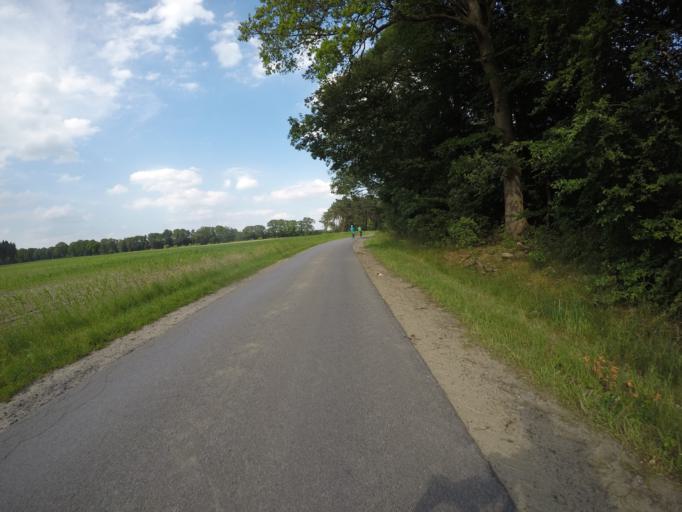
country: DE
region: North Rhine-Westphalia
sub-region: Regierungsbezirk Munster
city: Coesfeld
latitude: 51.8946
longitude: 7.1235
